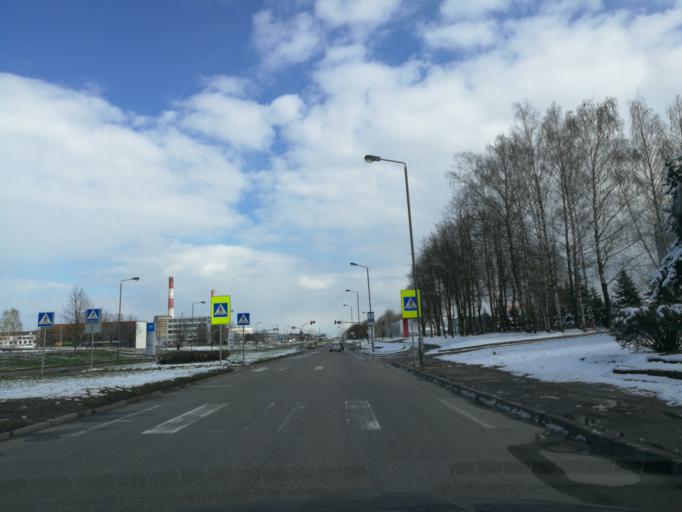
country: LT
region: Kauno apskritis
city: Dainava (Kaunas)
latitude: 54.9186
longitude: 23.9997
